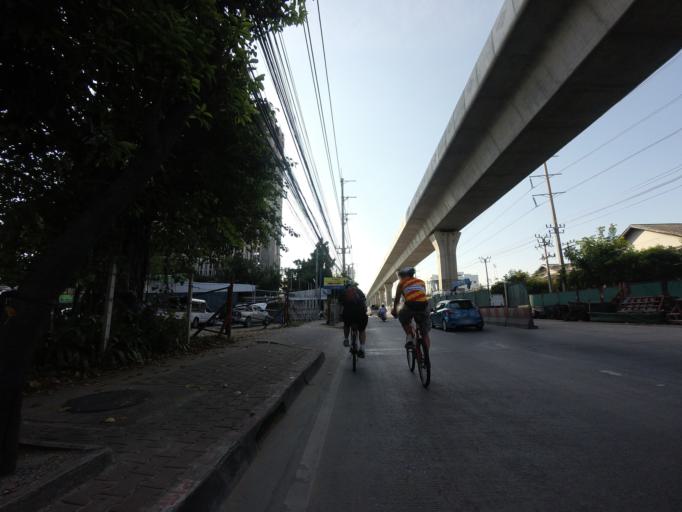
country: TH
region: Samut Prakan
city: Samut Prakan
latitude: 13.6056
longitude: 100.5961
